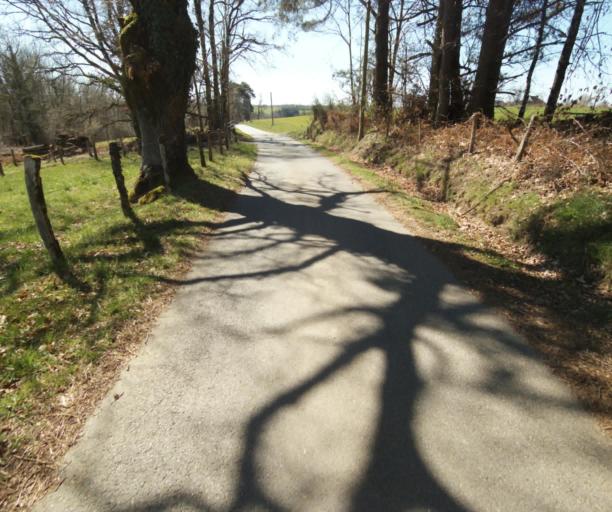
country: FR
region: Limousin
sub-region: Departement de la Correze
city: Chamboulive
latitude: 45.4592
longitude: 1.7095
